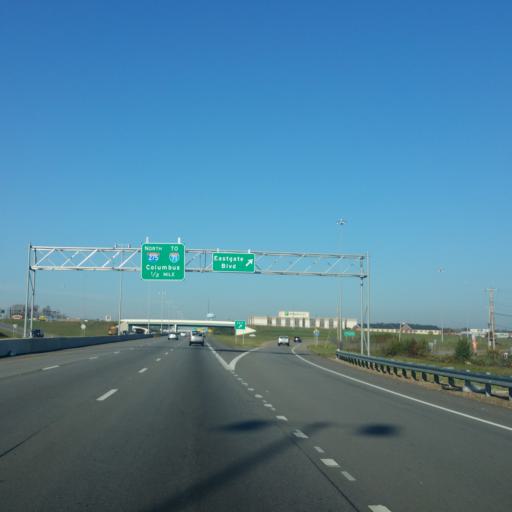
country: US
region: Ohio
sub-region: Clermont County
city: Summerside
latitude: 39.0969
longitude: -84.2691
